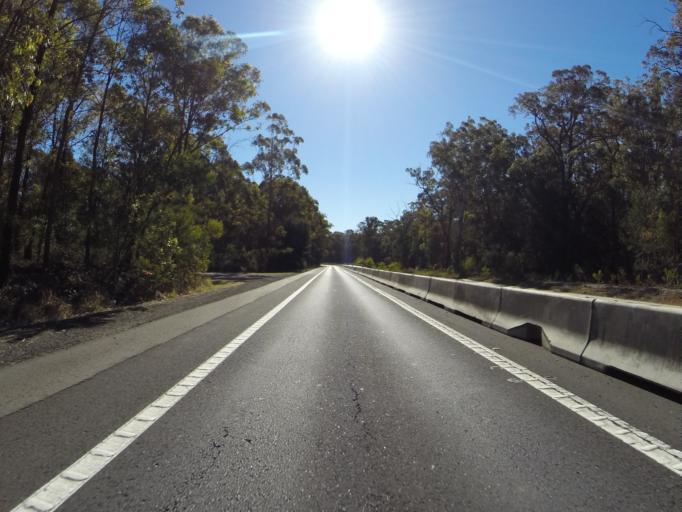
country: AU
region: New South Wales
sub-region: Wollondilly
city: Douglas Park
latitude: -34.2790
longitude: 150.7145
